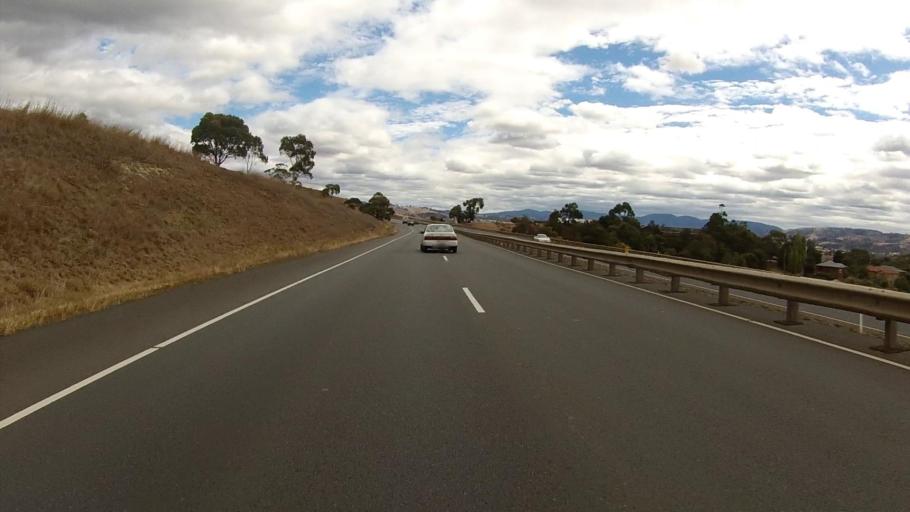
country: AU
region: Tasmania
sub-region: Glenorchy
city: Austins Ferry
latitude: -42.7664
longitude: 147.2351
